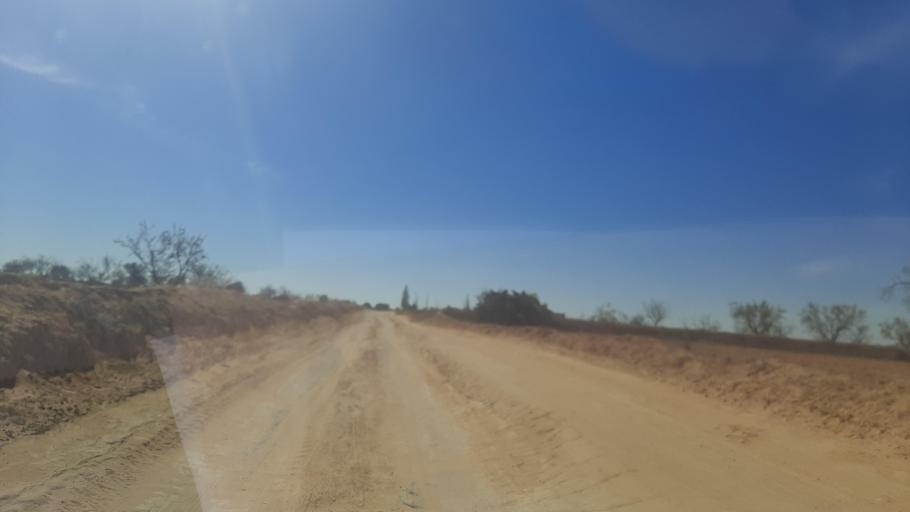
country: TN
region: Safaqis
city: Sfax
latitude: 34.8509
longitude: 10.5623
